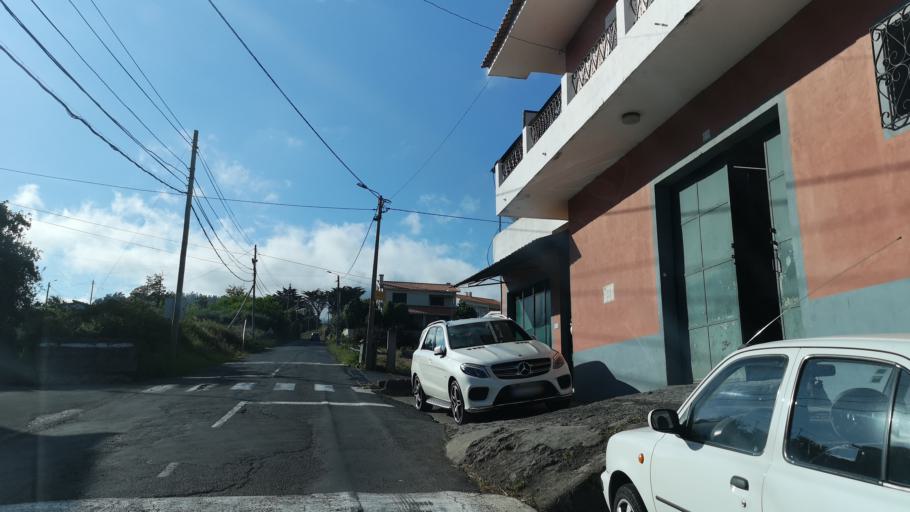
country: PT
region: Madeira
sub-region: Santa Cruz
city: Camacha
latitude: 32.6685
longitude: -16.8425
